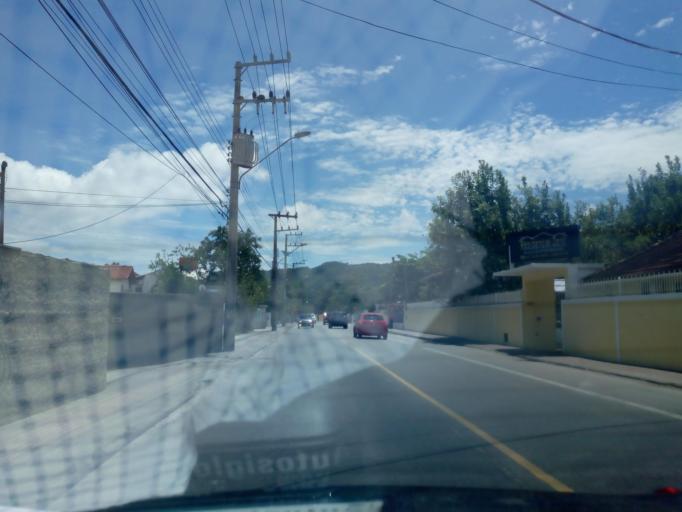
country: BR
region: Santa Catarina
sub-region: Florianopolis
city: Itacorubi
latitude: -27.4200
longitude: -48.4325
